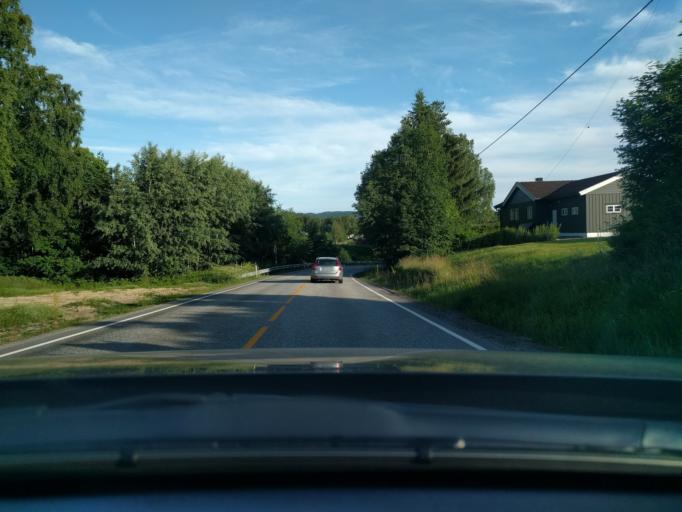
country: NO
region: Buskerud
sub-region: Kongsberg
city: Hvittingfoss
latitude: 59.4895
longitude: 10.0143
